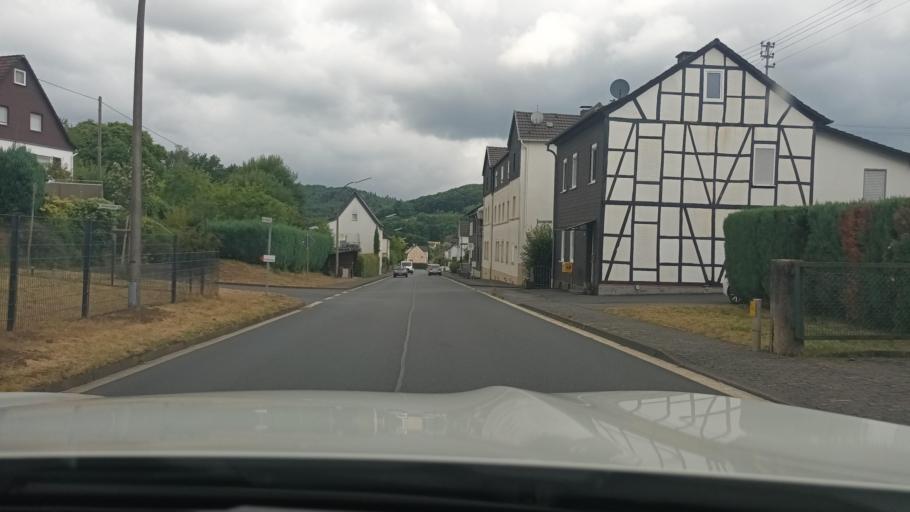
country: DE
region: North Rhine-Westphalia
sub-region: Regierungsbezirk Koln
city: Eitorf
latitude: 50.7733
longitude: 7.4287
